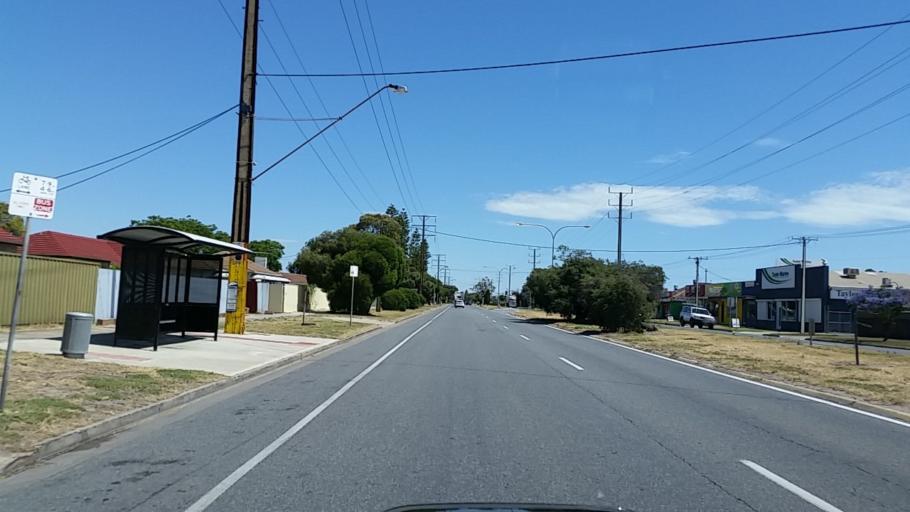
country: AU
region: South Australia
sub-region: Port Adelaide Enfield
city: Birkenhead
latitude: -34.8031
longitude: 138.5015
